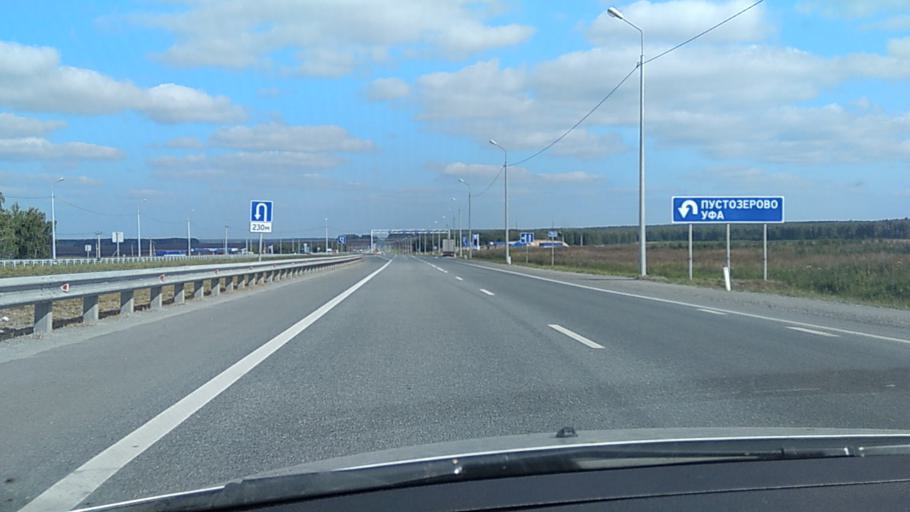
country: RU
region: Chelyabinsk
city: Chebarkul'
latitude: 54.9100
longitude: 60.4297
